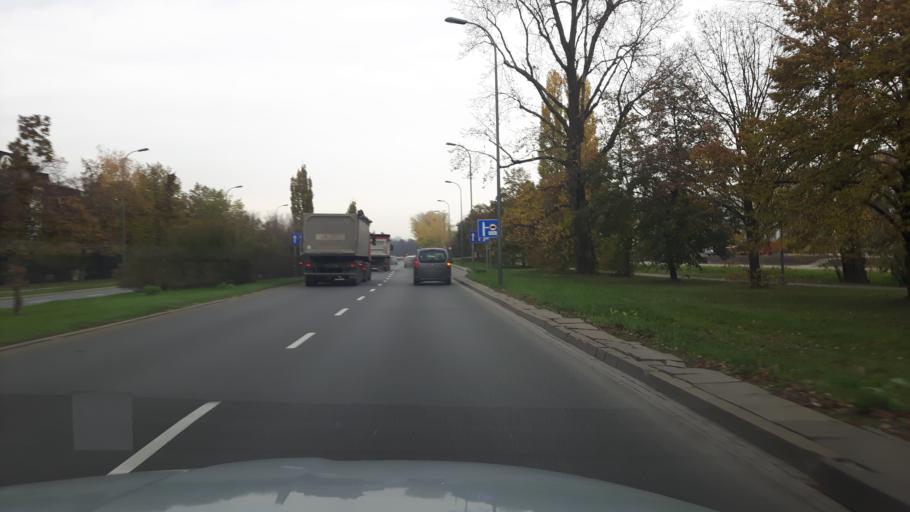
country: PL
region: Masovian Voivodeship
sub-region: Warszawa
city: Wilanow
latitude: 52.1676
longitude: 21.0772
